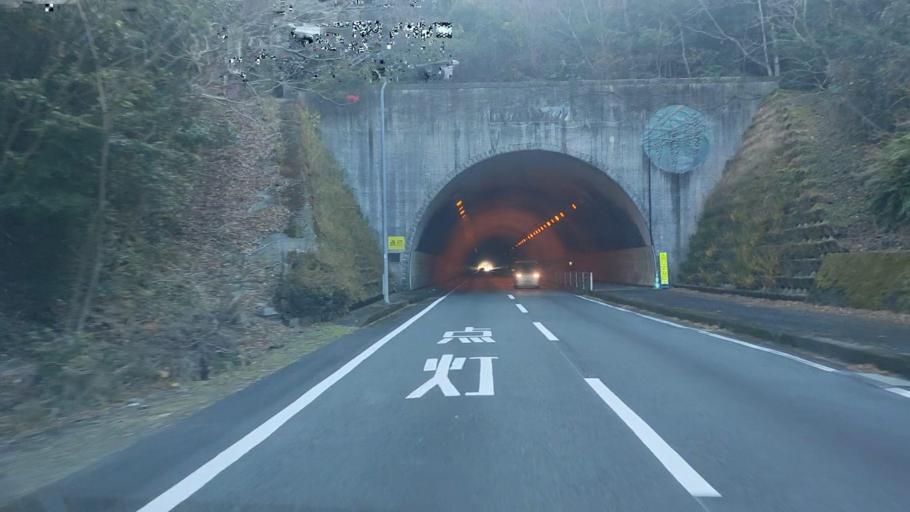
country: JP
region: Miyazaki
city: Nobeoka
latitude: 32.6866
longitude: 131.7920
